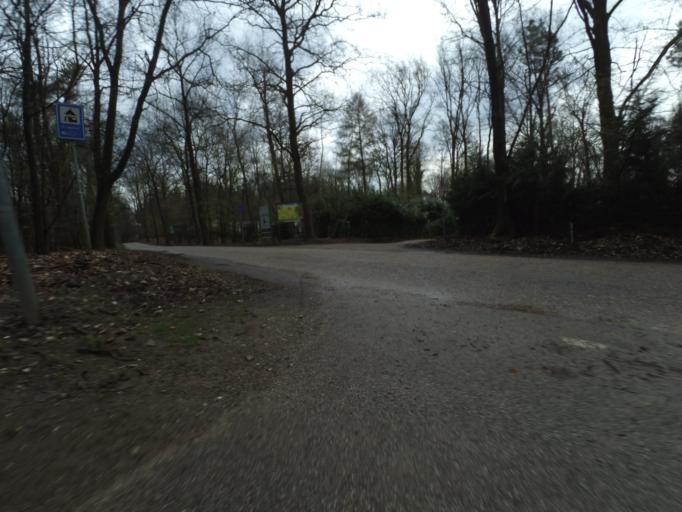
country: NL
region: Gelderland
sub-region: Gemeente Apeldoorn
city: Beekbergen
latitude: 52.1236
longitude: 5.9289
